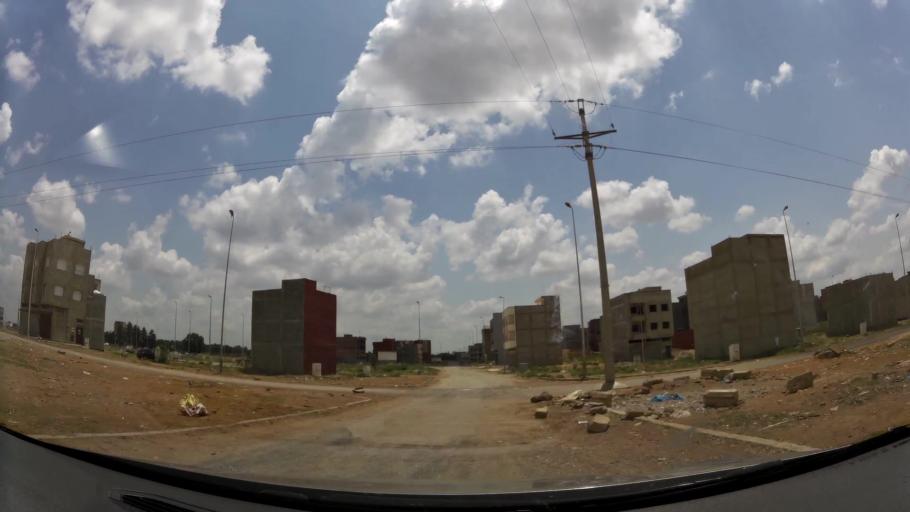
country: MA
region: Rabat-Sale-Zemmour-Zaer
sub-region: Khemisset
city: Tiflet
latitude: 34.0014
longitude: -6.5242
